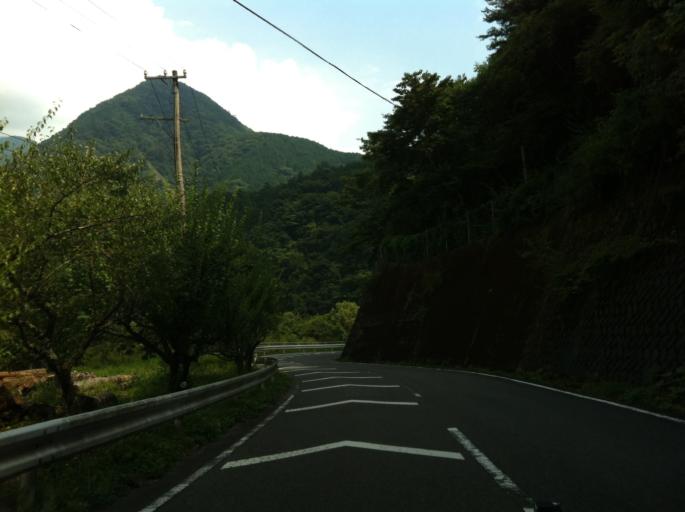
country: JP
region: Shizuoka
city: Shizuoka-shi
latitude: 35.2411
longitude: 138.3417
